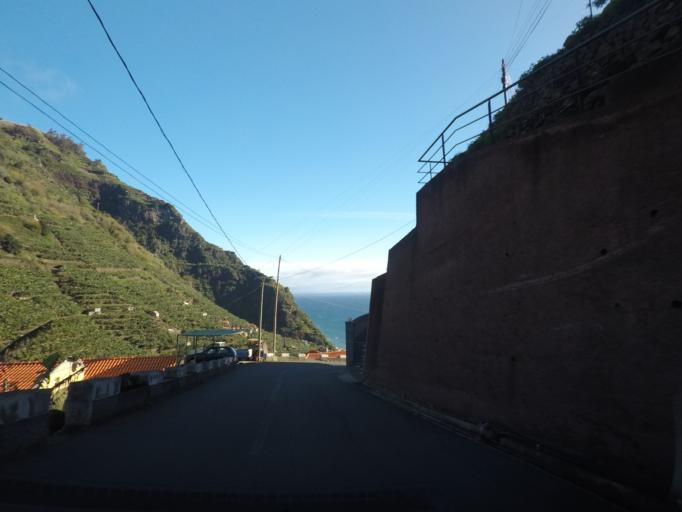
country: PT
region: Madeira
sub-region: Calheta
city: Arco da Calheta
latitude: 32.7074
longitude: -17.1349
